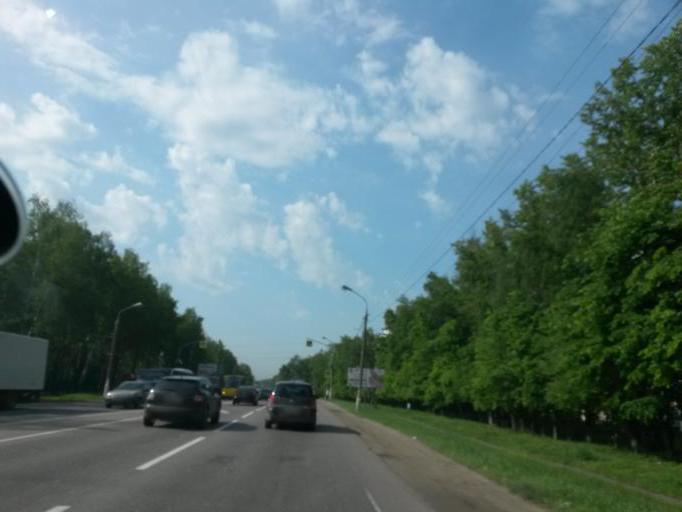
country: RU
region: Moskovskaya
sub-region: Chekhovskiy Rayon
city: Chekhov
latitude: 55.1717
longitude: 37.4713
